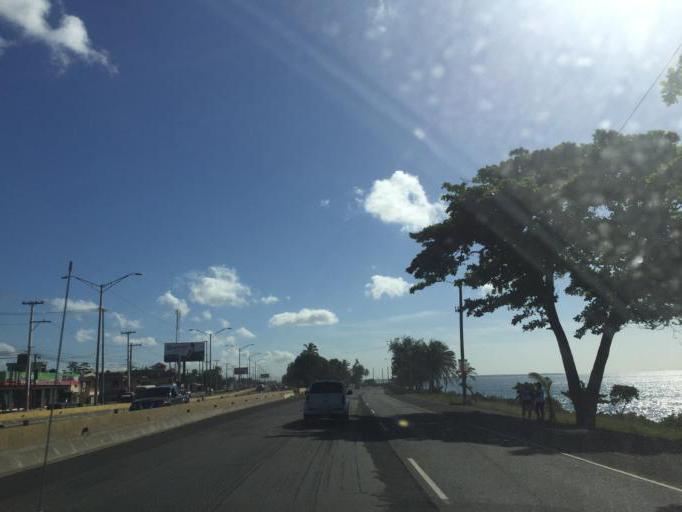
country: DO
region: Santo Domingo
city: Guerra
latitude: 18.4621
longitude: -69.7358
